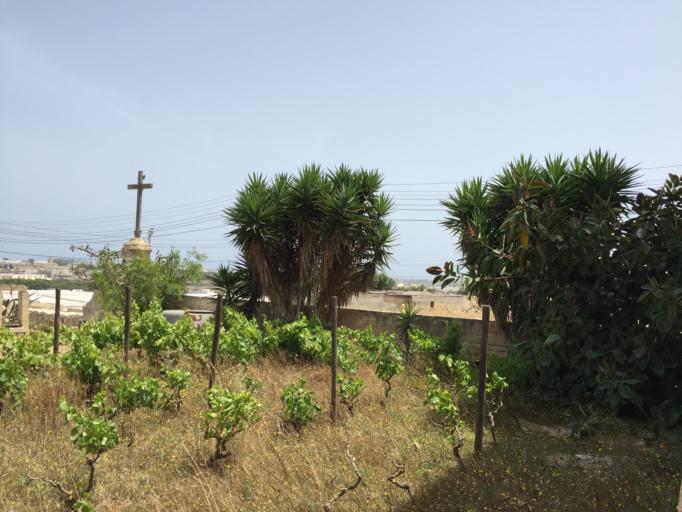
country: MT
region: Hal Ghaxaq
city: Ghaxaq
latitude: 35.8544
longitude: 14.5161
